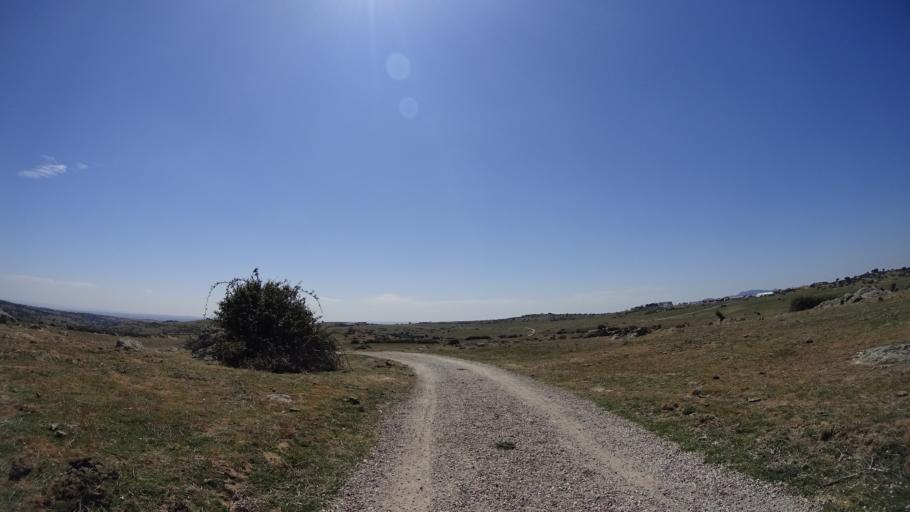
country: ES
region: Madrid
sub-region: Provincia de Madrid
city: Colmenar Viejo
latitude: 40.7026
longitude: -3.7517
